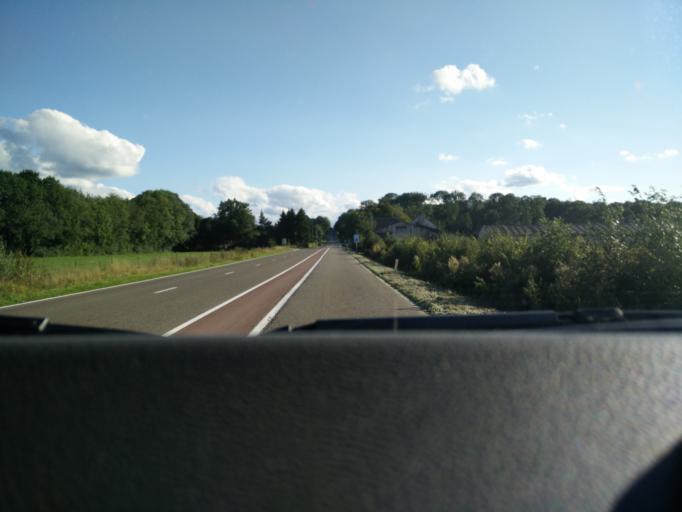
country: BE
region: Wallonia
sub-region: Province du Hainaut
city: Beaumont
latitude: 50.1930
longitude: 4.2212
